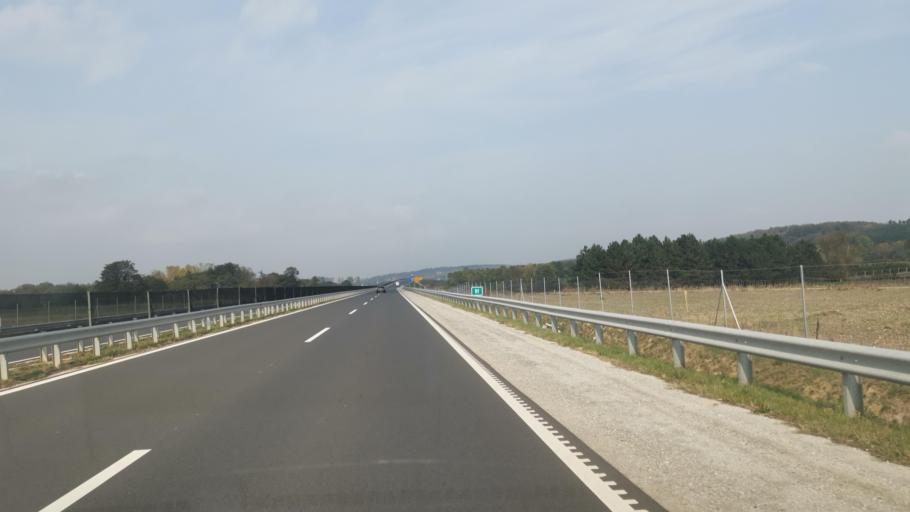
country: AT
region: Burgenland
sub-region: Politischer Bezirk Oberpullendorf
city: Deutschkreutz
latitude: 47.6464
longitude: 16.6273
